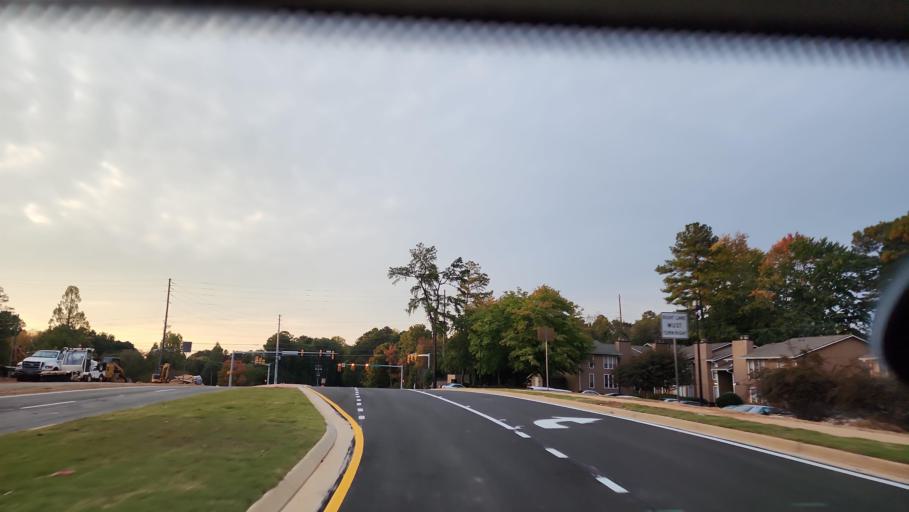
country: US
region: Georgia
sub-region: Cobb County
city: Vinings
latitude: 33.9130
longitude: -84.4706
